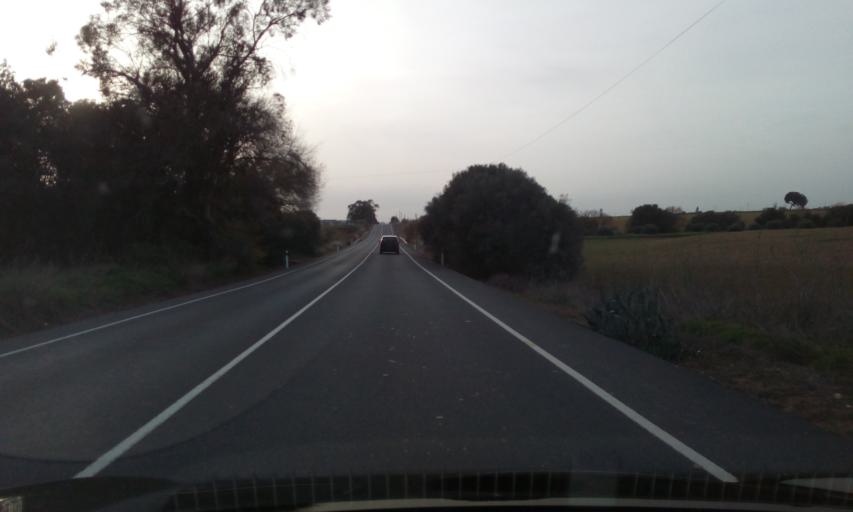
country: ES
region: Andalusia
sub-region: Provincia de Huelva
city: Lucena del Puerto
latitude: 37.3270
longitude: -6.7810
